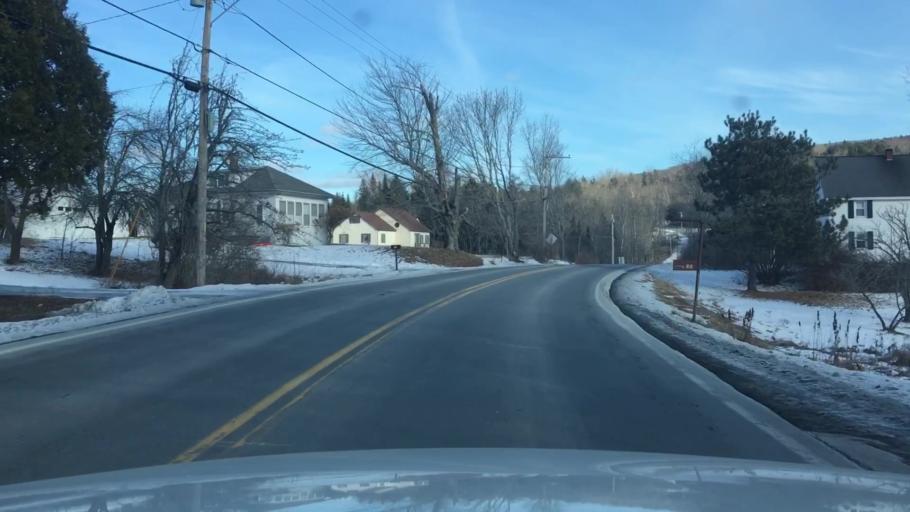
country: US
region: Maine
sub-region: Penobscot County
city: Holden
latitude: 44.7383
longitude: -68.6260
